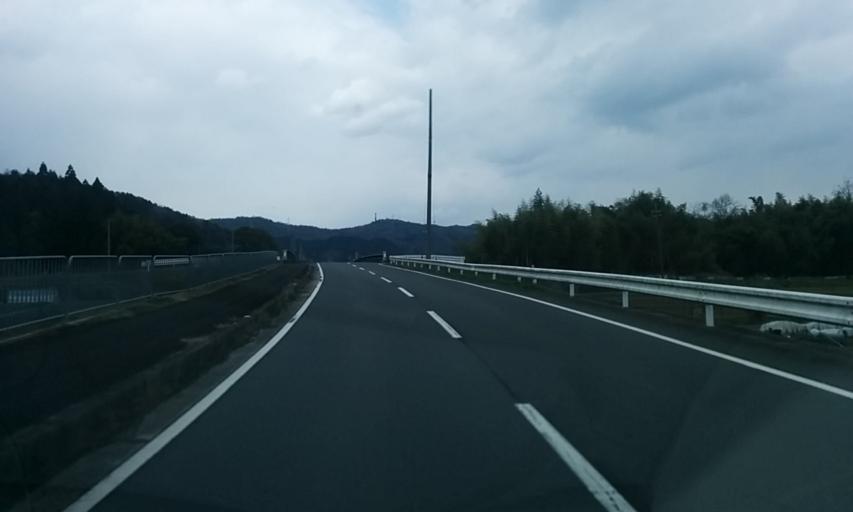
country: JP
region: Kyoto
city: Kameoka
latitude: 35.0917
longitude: 135.4446
